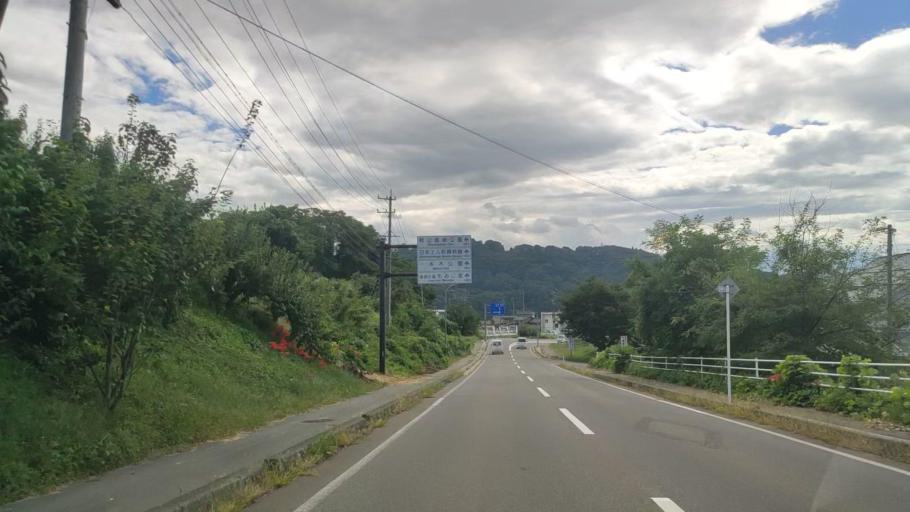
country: JP
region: Nagano
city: Nakano
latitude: 36.7752
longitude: 138.3249
